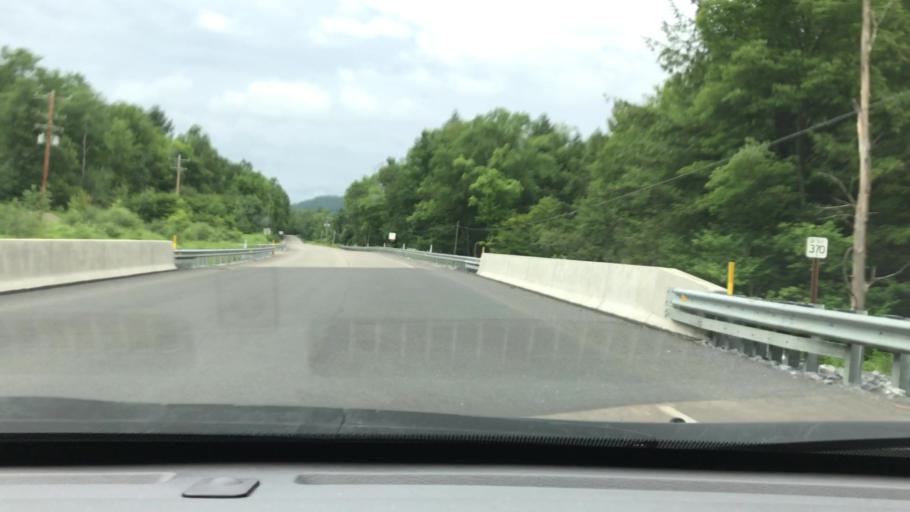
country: US
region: Pennsylvania
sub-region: McKean County
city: Bradford
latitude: 41.8498
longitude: -78.6794
